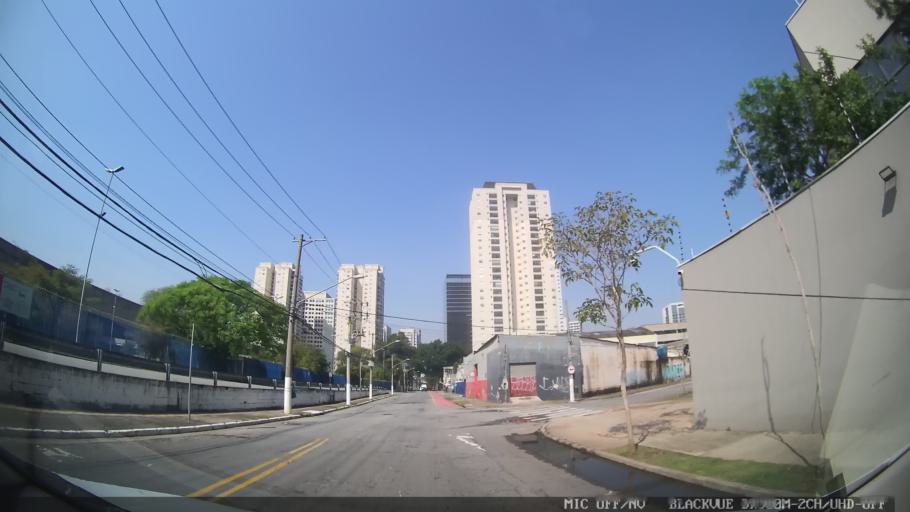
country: BR
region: Sao Paulo
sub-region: Sao Paulo
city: Sao Paulo
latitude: -23.5187
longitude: -46.6615
